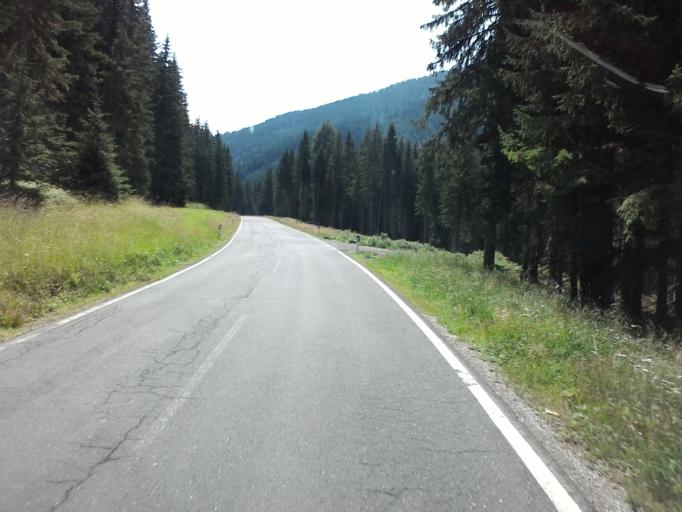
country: AT
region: Tyrol
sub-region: Politischer Bezirk Lienz
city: Obertilliach
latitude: 46.7127
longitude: 12.5783
